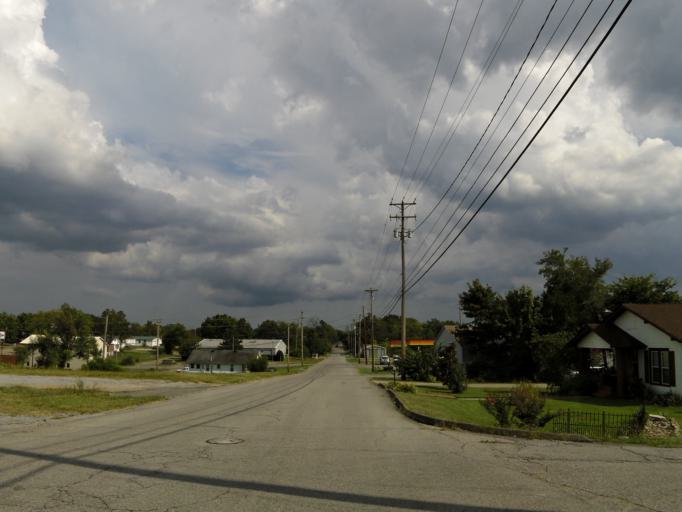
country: US
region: Tennessee
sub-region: Dickson County
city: Dickson
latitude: 36.0854
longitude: -87.3994
